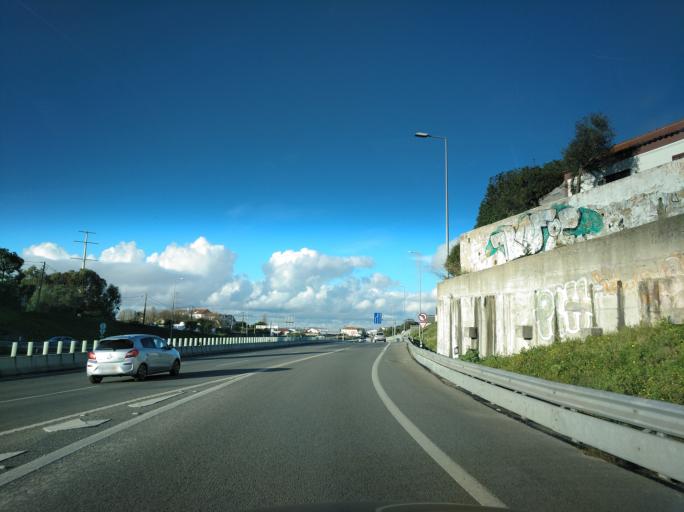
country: PT
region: Setubal
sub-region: Almada
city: Sobreda
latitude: 38.6482
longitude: -9.2005
